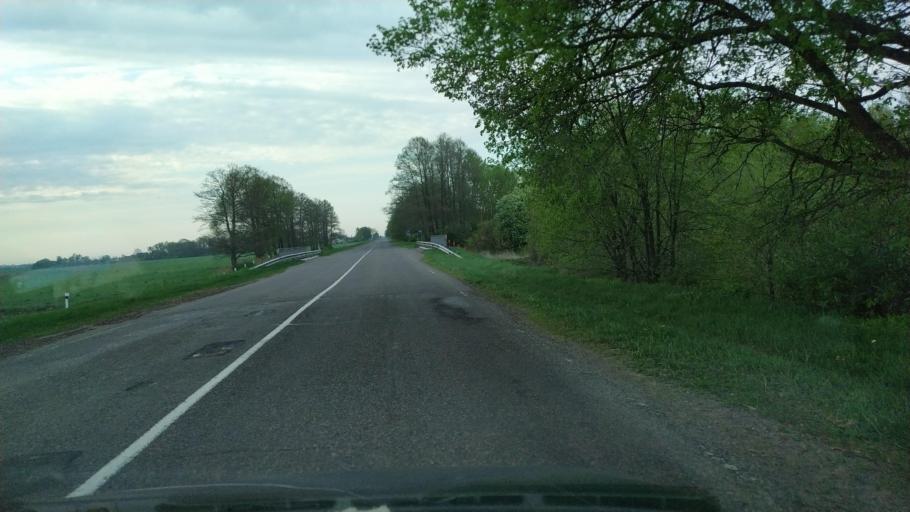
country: BY
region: Brest
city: Zhabinka
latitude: 52.2349
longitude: 23.9811
